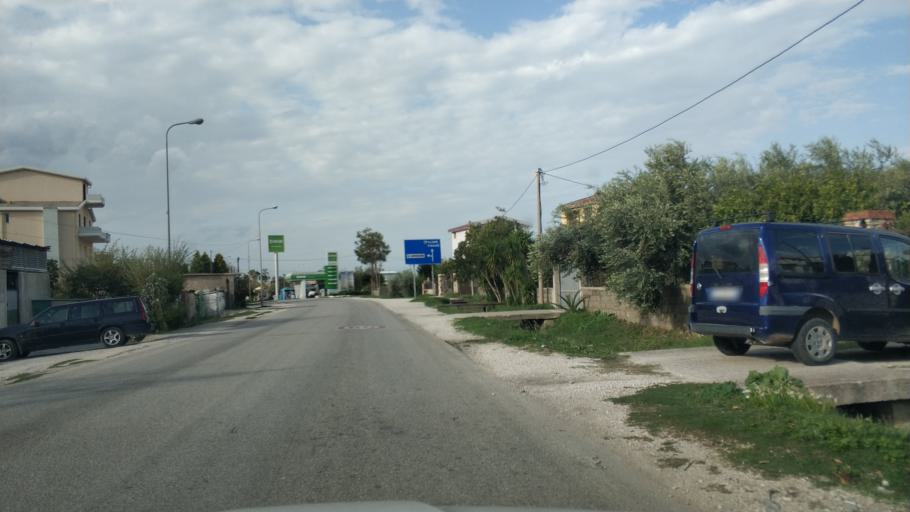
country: AL
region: Vlore
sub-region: Rrethi i Vlores
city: Orikum
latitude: 40.3281
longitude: 19.4784
